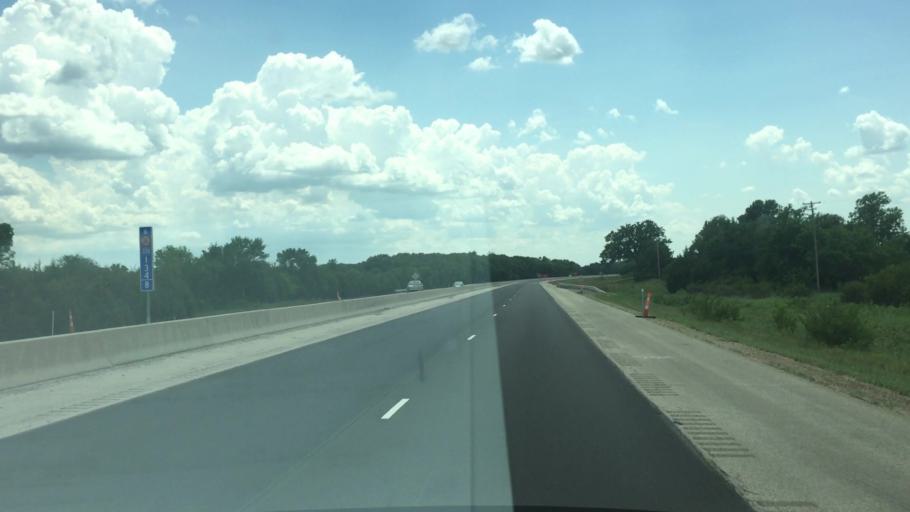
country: US
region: Kansas
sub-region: Lyon County
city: Emporia
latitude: 38.5054
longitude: -96.1506
